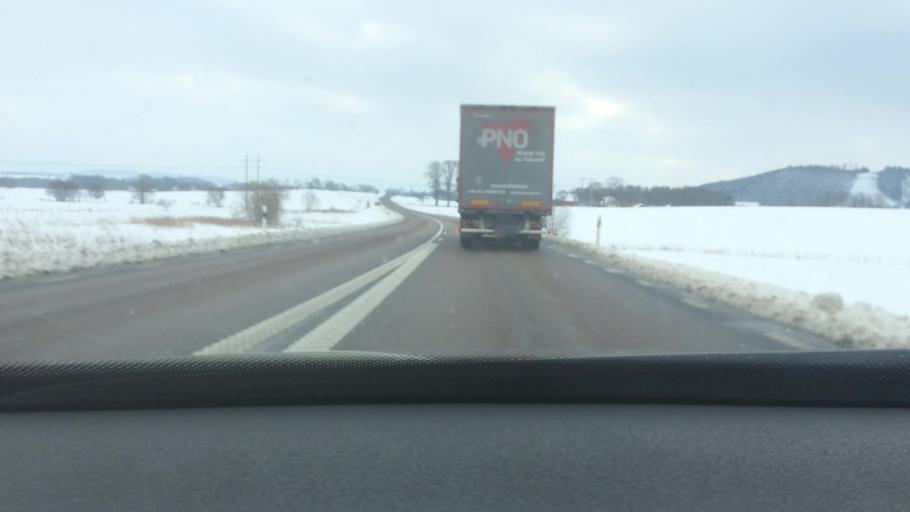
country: SE
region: Vaestra Goetaland
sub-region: Falkopings Kommun
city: Falkoeping
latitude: 58.2072
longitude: 13.5604
